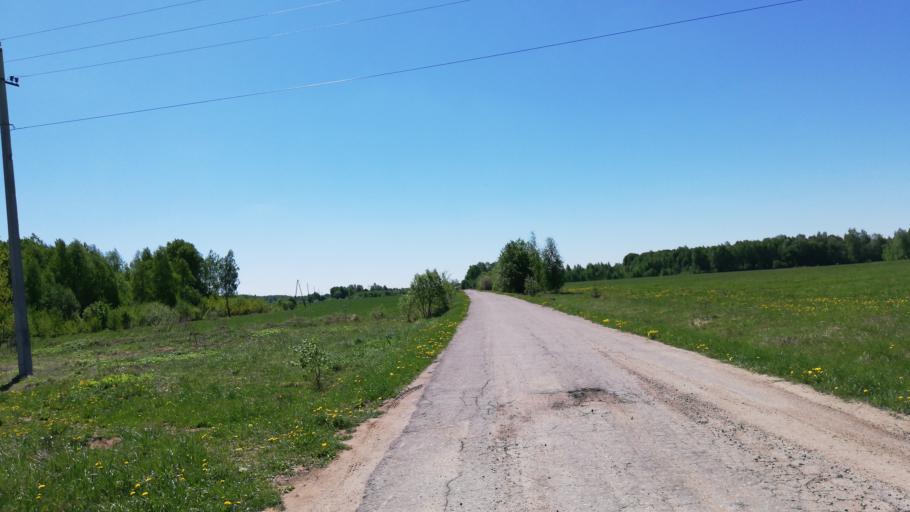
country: RU
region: Ivanovo
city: Pistsovo
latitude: 57.1242
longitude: 40.6004
